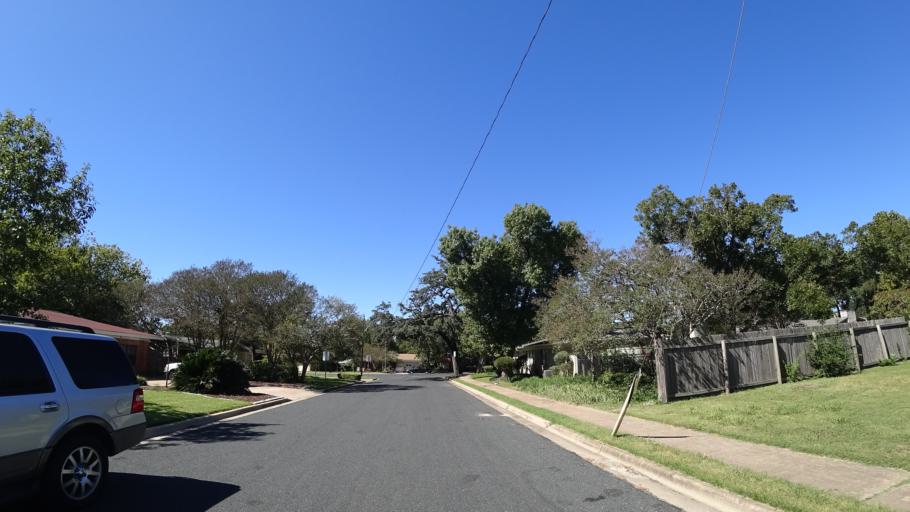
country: US
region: Texas
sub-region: Travis County
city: Rollingwood
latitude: 30.2285
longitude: -97.7931
